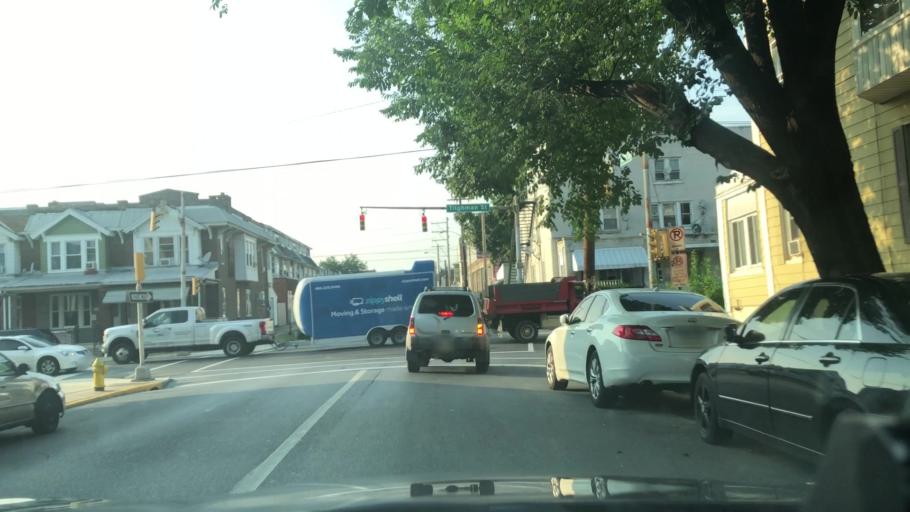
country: US
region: Pennsylvania
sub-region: Lehigh County
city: Allentown
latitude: 40.6098
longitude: -75.4823
